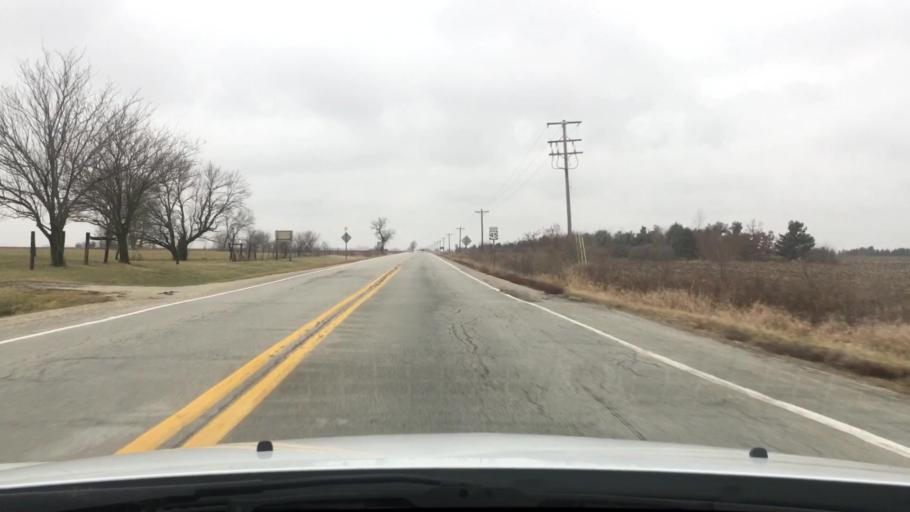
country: US
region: Illinois
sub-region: Iroquois County
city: Clifton
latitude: 40.8872
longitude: -87.8664
